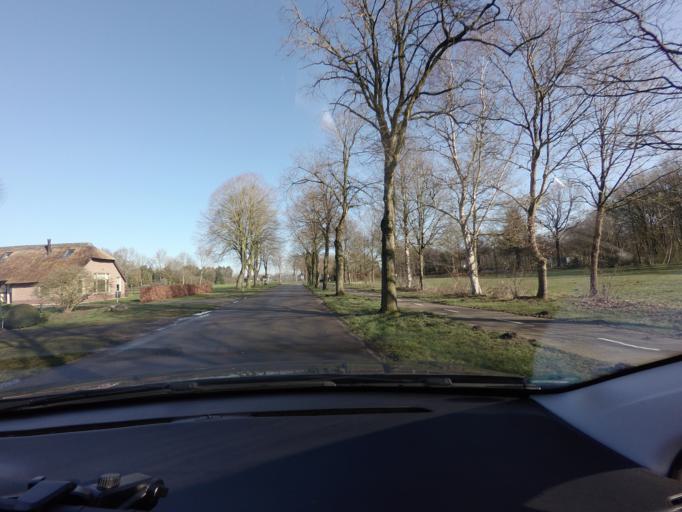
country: NL
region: Drenthe
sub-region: Gemeente Assen
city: Assen
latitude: 52.8755
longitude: 6.5880
